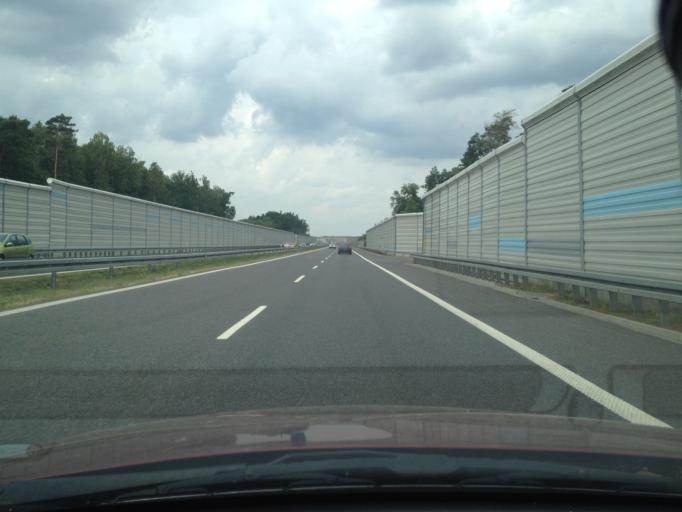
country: PL
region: West Pomeranian Voivodeship
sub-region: Powiat pyrzycki
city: Lipiany
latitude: 52.9661
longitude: 14.9178
